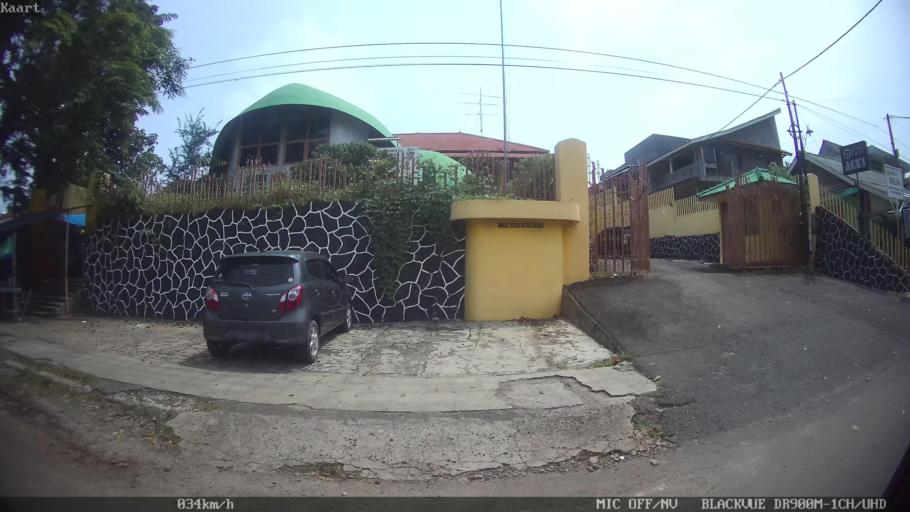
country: ID
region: Lampung
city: Bandarlampung
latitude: -5.4424
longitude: 105.2656
